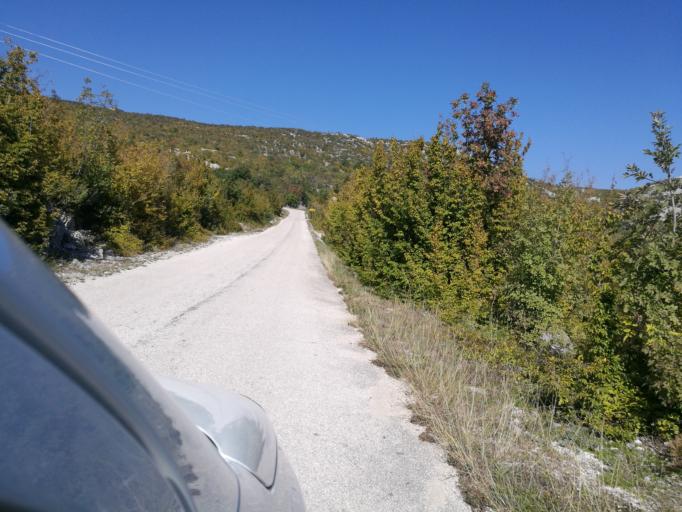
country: HR
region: Splitsko-Dalmatinska
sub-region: Grad Omis
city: Omis
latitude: 43.5156
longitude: 16.7277
